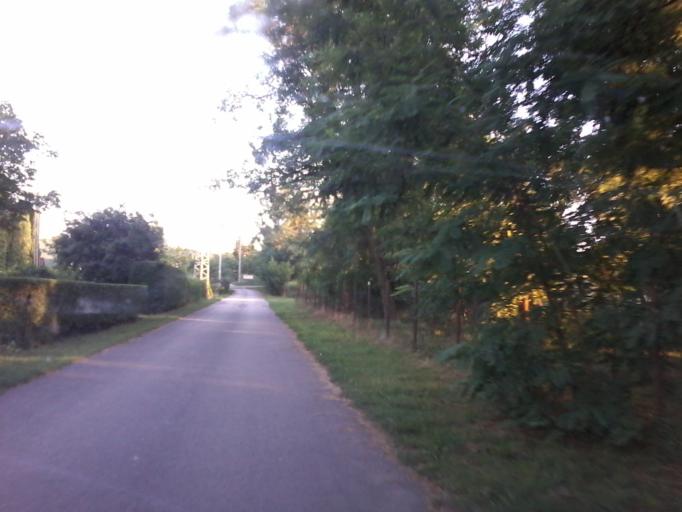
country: HU
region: Vas
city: Janoshaza
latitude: 47.1596
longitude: 17.0988
